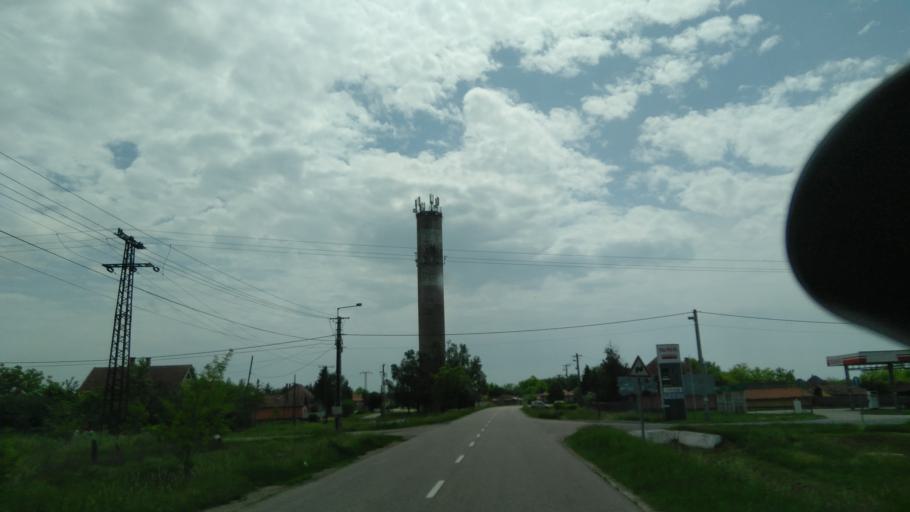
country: HU
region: Hajdu-Bihar
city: Komadi
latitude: 47.0144
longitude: 21.4978
